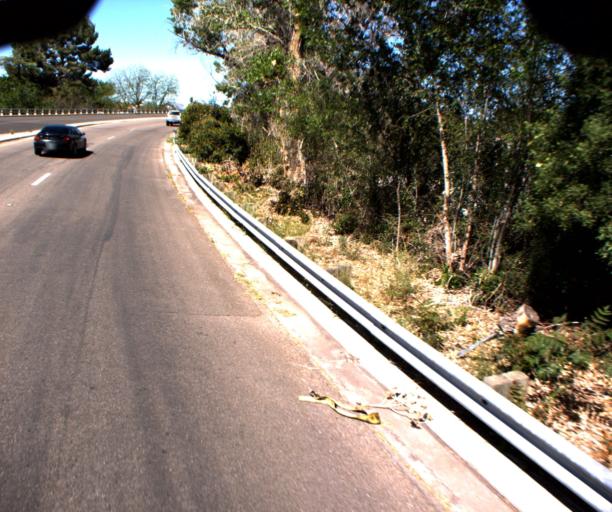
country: US
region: Arizona
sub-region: Santa Cruz County
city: Nogales
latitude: 31.3490
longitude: -110.9254
